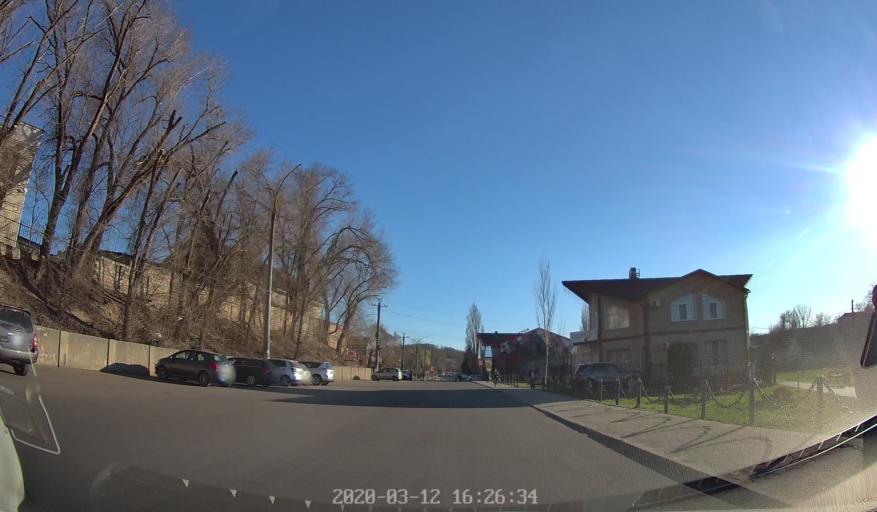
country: MD
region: Anenii Noi
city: Anenii Noi
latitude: 46.8809
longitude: 29.2325
